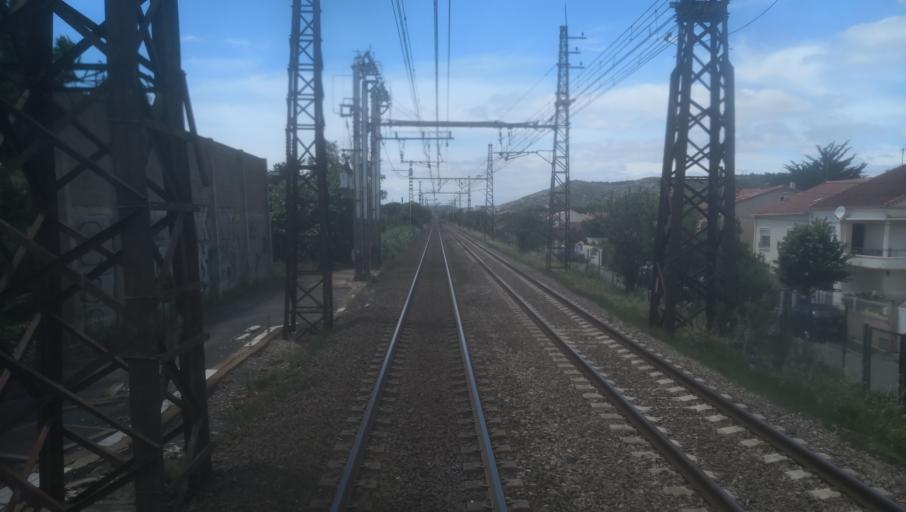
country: FR
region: Languedoc-Roussillon
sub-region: Departement de l'Aude
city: Narbonne
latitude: 43.1807
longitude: 2.9803
